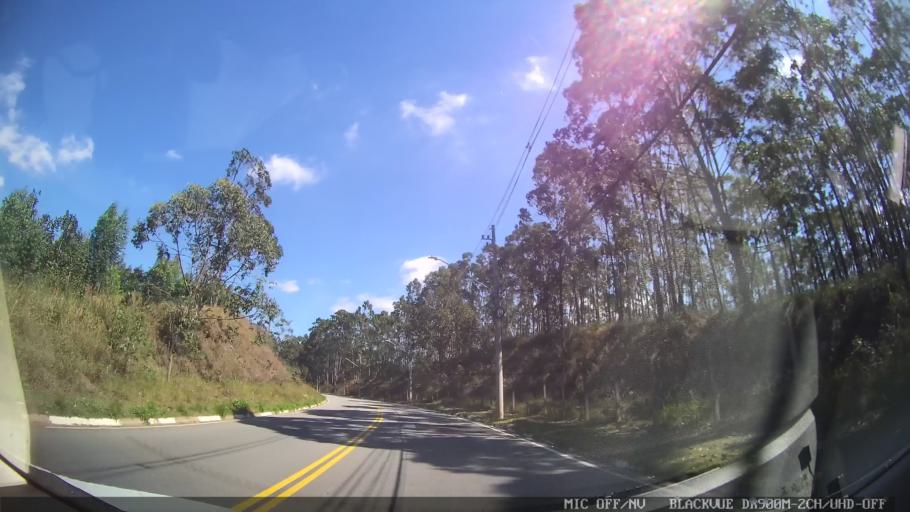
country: BR
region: Sao Paulo
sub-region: Barueri
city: Barueri
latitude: -23.4505
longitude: -46.8381
